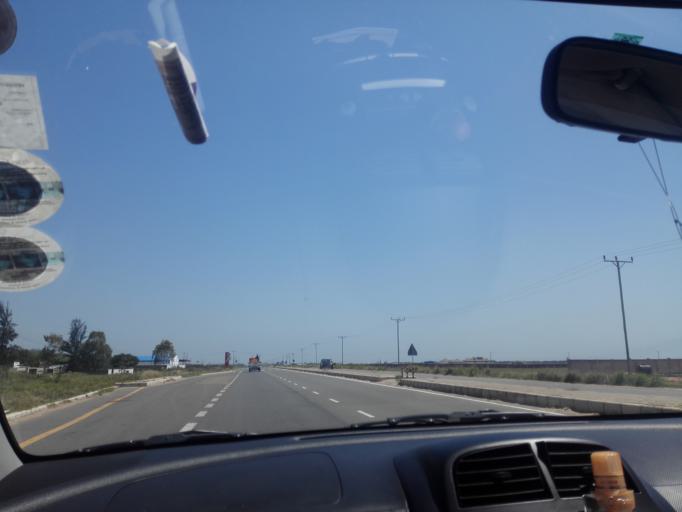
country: MZ
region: Maputo City
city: Maputo
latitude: -25.8457
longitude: 32.6714
